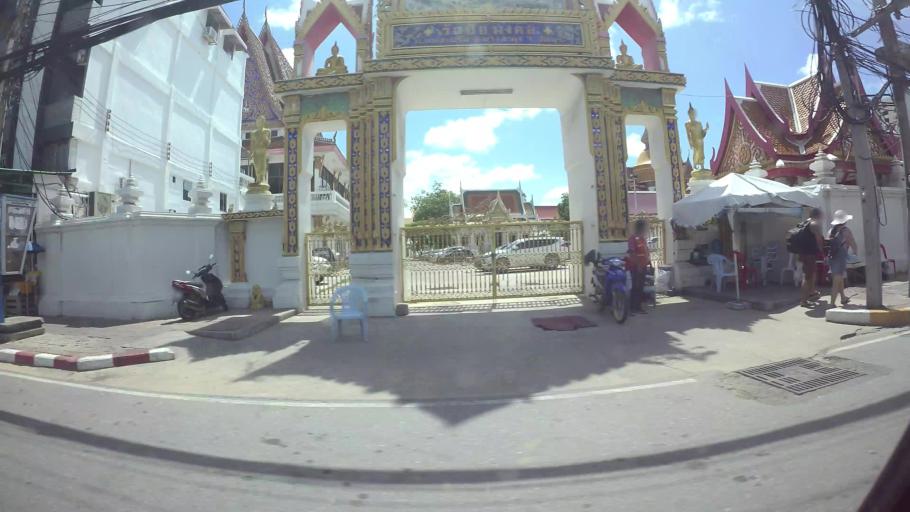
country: TH
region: Chon Buri
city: Phatthaya
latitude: 12.9258
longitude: 100.8759
